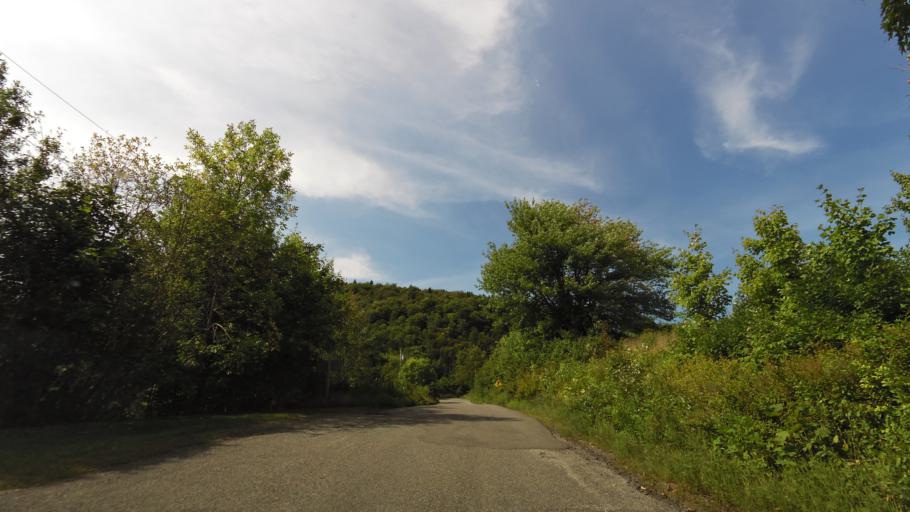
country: CA
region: New Brunswick
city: Hampton
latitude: 45.5490
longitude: -65.8357
